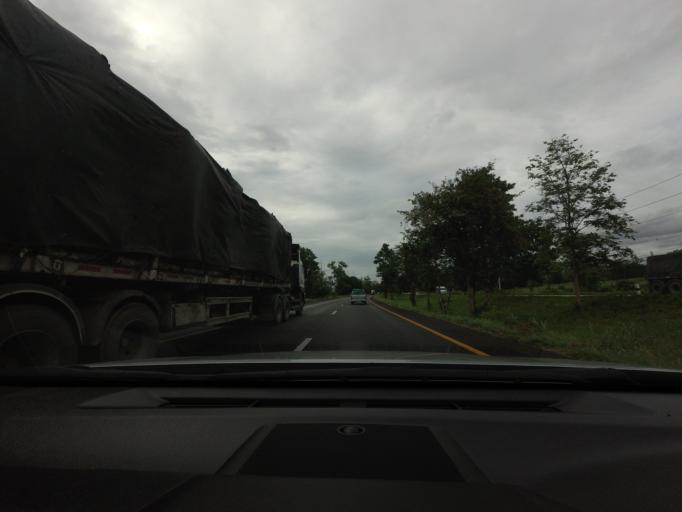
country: TH
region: Prachuap Khiri Khan
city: Hua Hin
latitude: 12.6292
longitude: 99.8574
